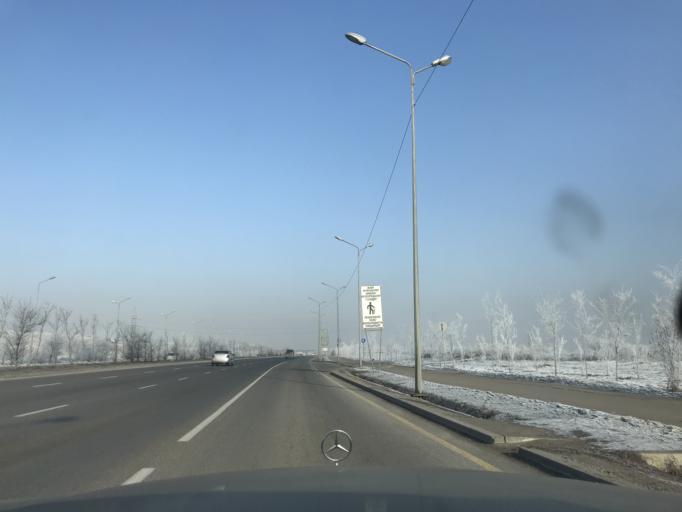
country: KZ
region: Almaty Oblysy
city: Burunday
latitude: 43.3309
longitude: 76.8337
